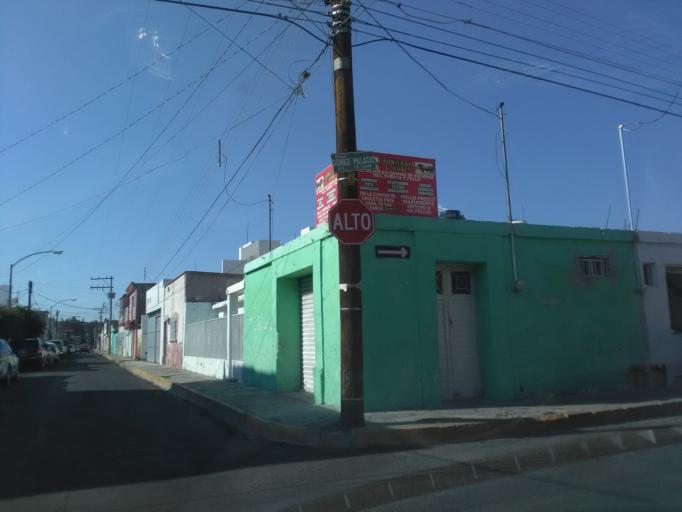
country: MX
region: Durango
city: Victoria de Durango
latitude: 24.0321
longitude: -104.6632
